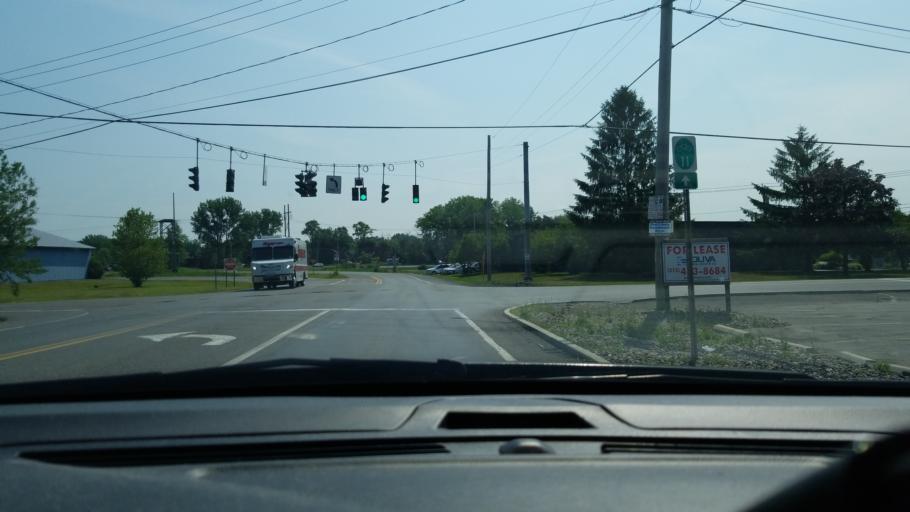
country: US
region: New York
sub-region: Onondaga County
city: East Syracuse
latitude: 43.1001
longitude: -76.0798
